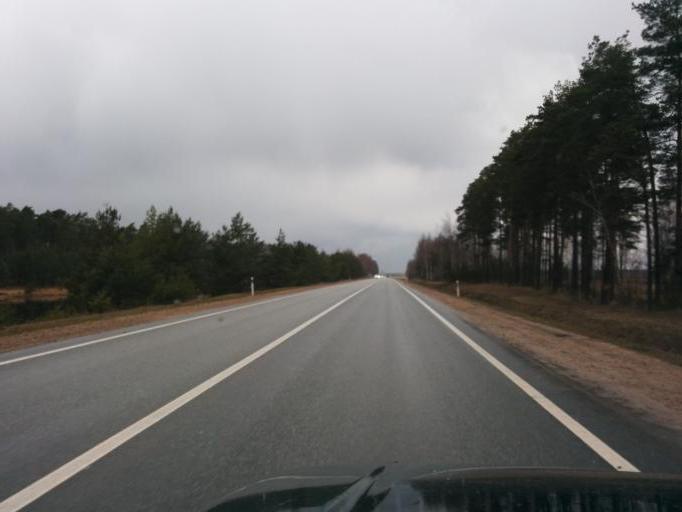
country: LV
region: Marupe
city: Marupe
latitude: 56.8463
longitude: 24.0145
